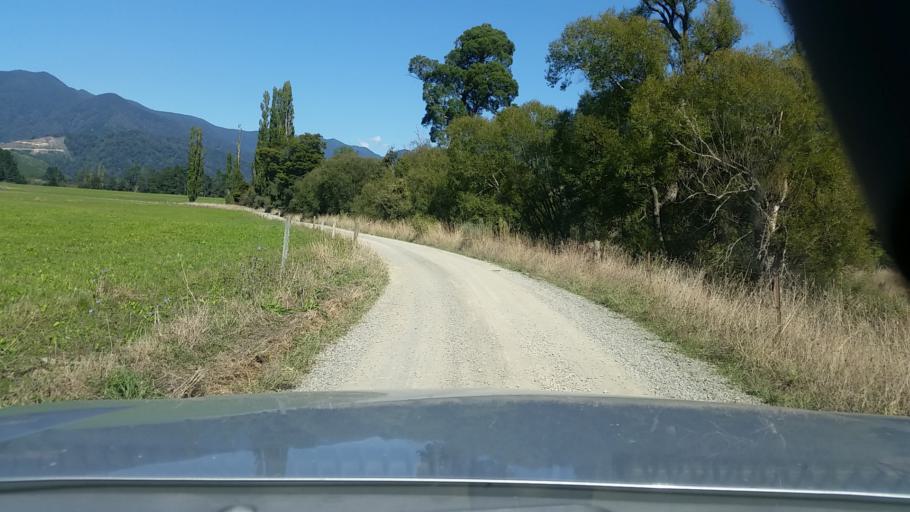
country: NZ
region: Nelson
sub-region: Nelson City
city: Nelson
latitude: -41.2667
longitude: 173.5760
